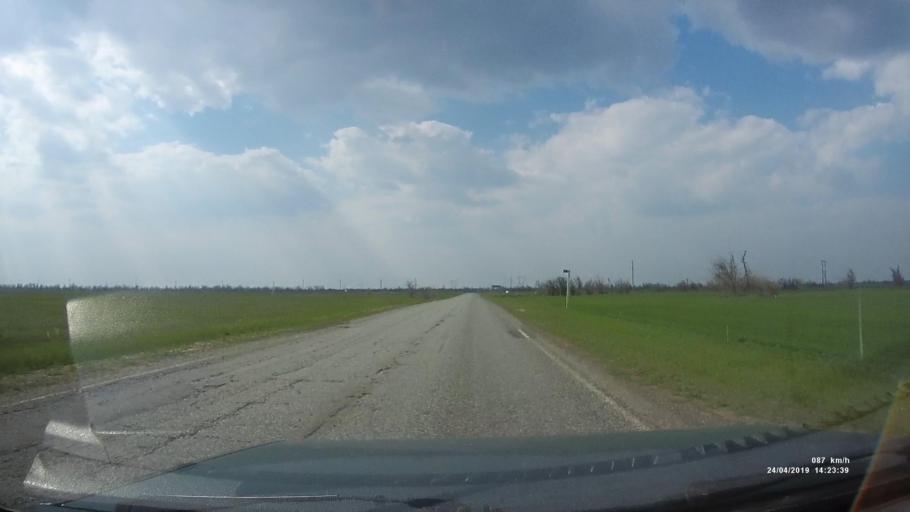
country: RU
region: Kalmykiya
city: Arshan'
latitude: 46.3239
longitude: 44.1114
